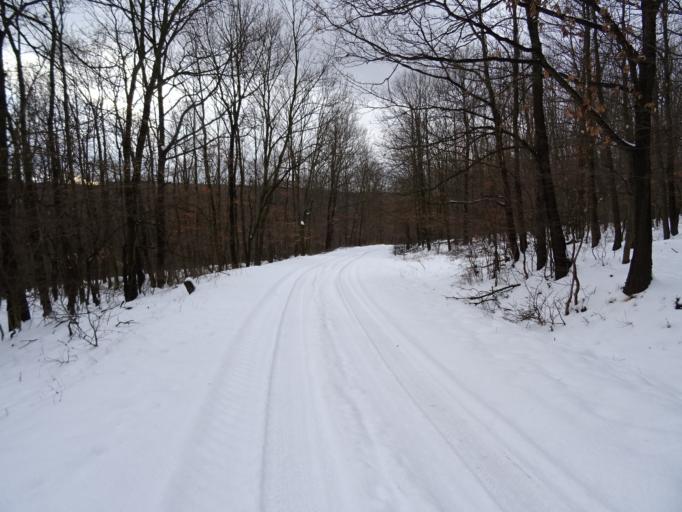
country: HU
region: Fejer
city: Szarliget
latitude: 47.4686
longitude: 18.4297
